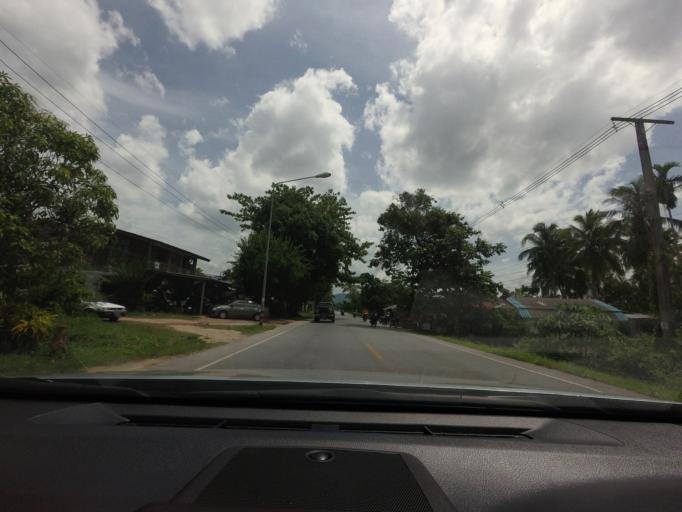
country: TH
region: Yala
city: Raman
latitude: 6.4635
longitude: 101.3783
